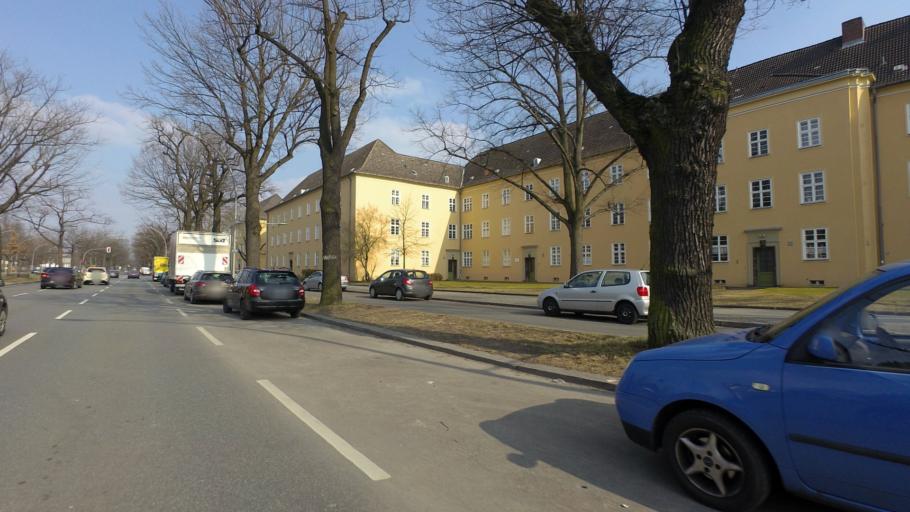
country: DE
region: Berlin
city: Dahlem
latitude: 52.4470
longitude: 13.2986
